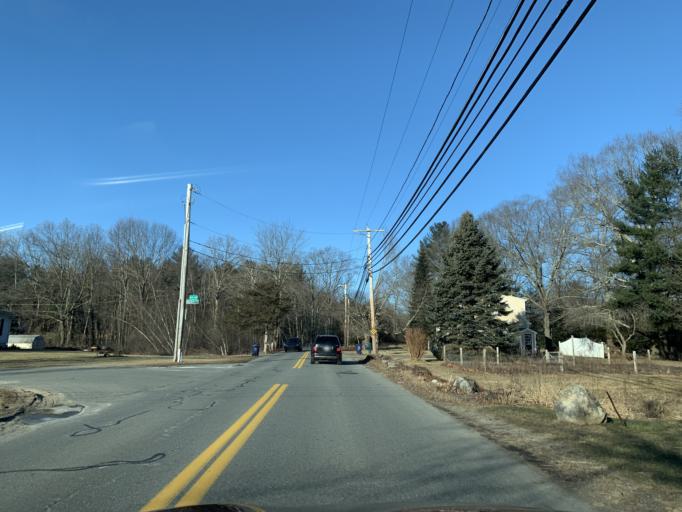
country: US
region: Massachusetts
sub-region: Middlesex County
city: Dracut
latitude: 42.7086
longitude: -71.2537
